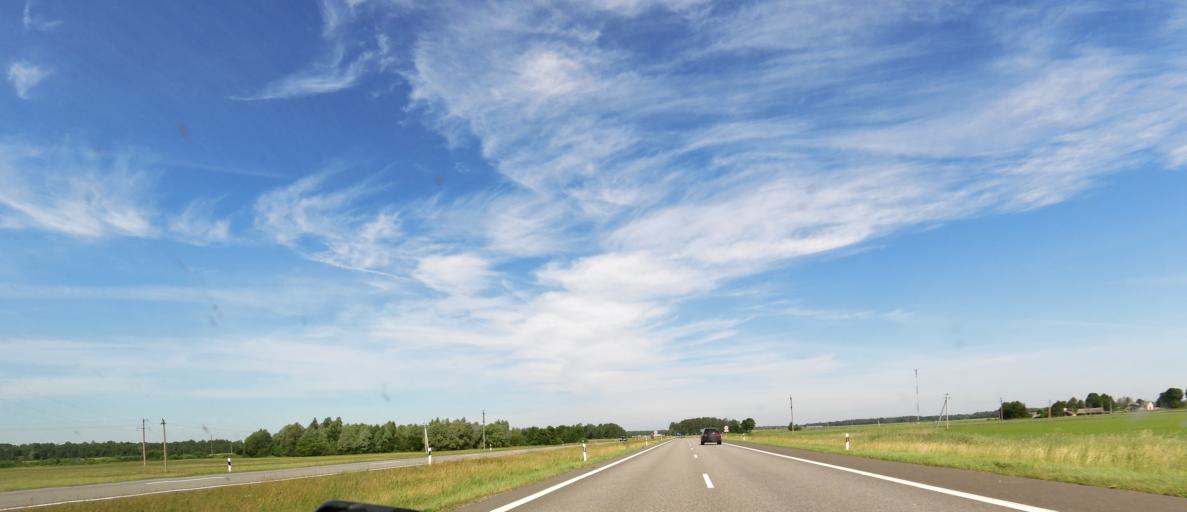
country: LT
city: Ramygala
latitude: 55.5482
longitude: 24.5249
